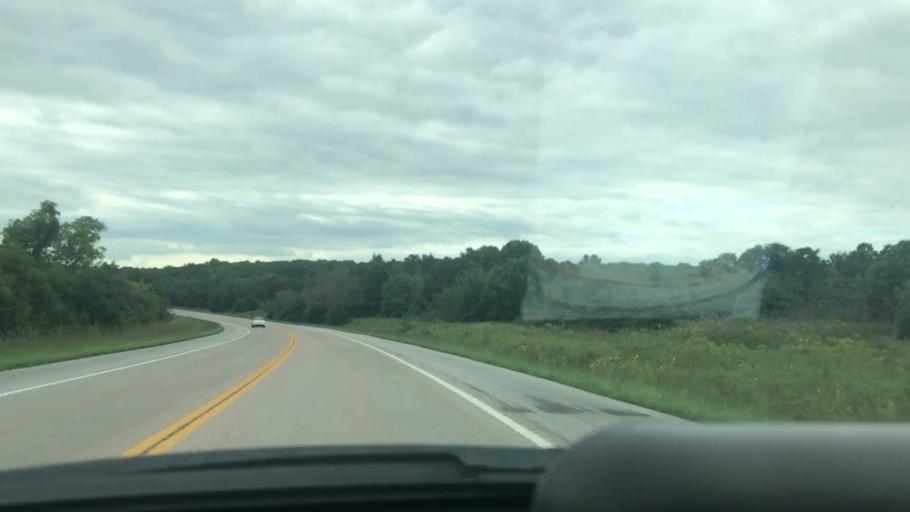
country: US
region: Missouri
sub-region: Benton County
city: Warsaw
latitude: 38.2071
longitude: -93.3289
